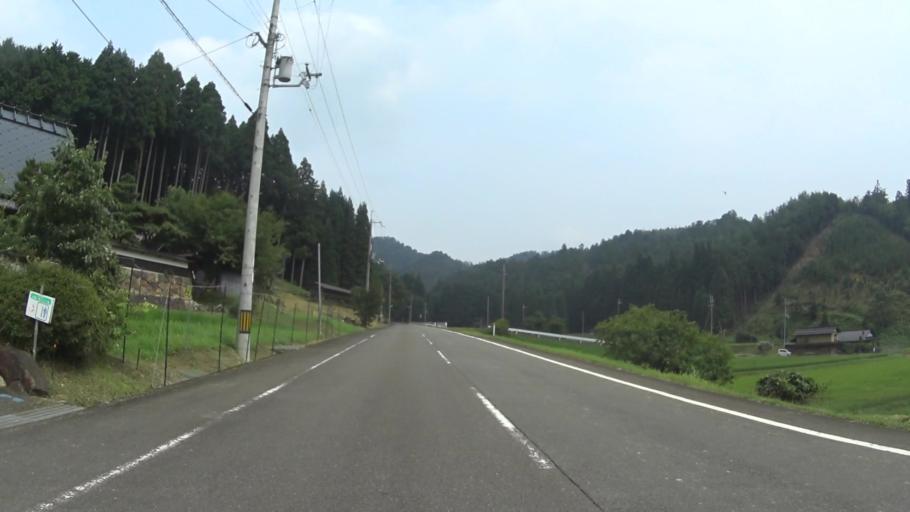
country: JP
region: Kyoto
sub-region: Kyoto-shi
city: Kamigyo-ku
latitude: 35.2047
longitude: 135.6555
